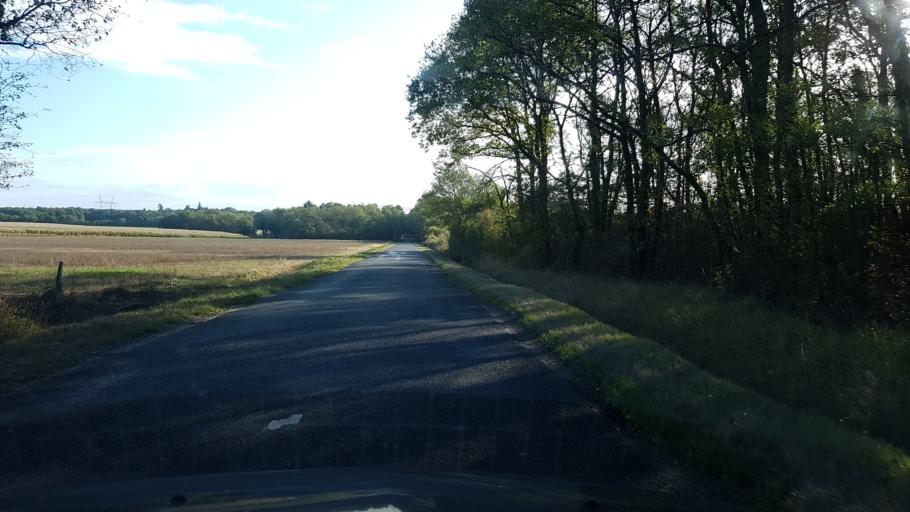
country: FR
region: Centre
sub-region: Departement du Loiret
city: Cerdon
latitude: 47.6951
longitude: 2.3778
